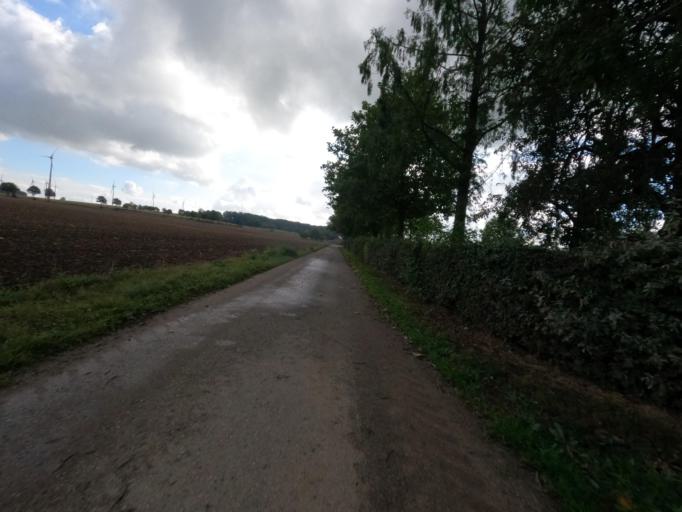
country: DE
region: North Rhine-Westphalia
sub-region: Regierungsbezirk Koln
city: Linnich
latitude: 51.0192
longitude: 6.2705
